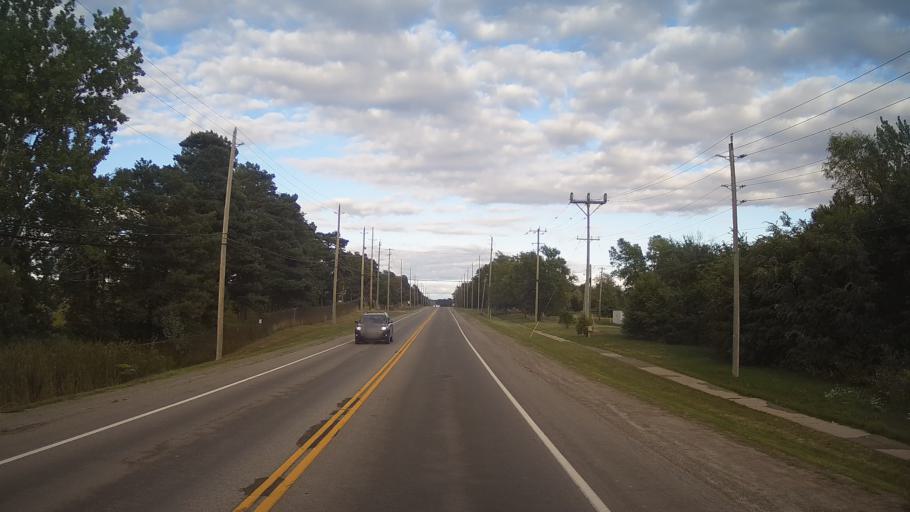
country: CA
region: Ontario
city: Kingston
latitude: 44.2404
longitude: -76.4509
